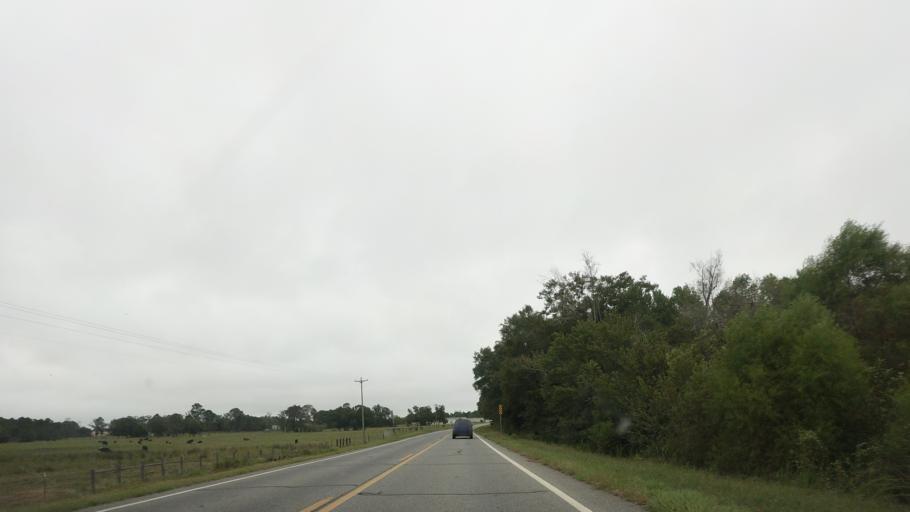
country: US
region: Georgia
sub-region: Irwin County
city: Ocilla
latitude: 31.5737
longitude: -83.2530
